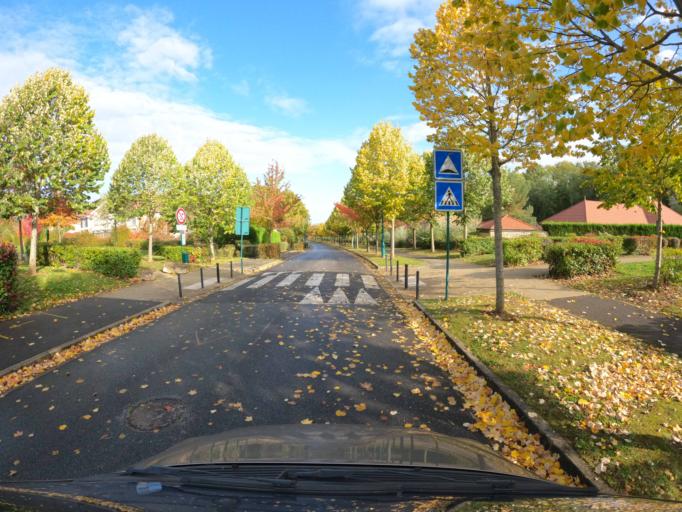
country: FR
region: Ile-de-France
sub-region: Departement de Seine-et-Marne
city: Magny-le-Hongre
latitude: 48.8639
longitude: 2.8233
